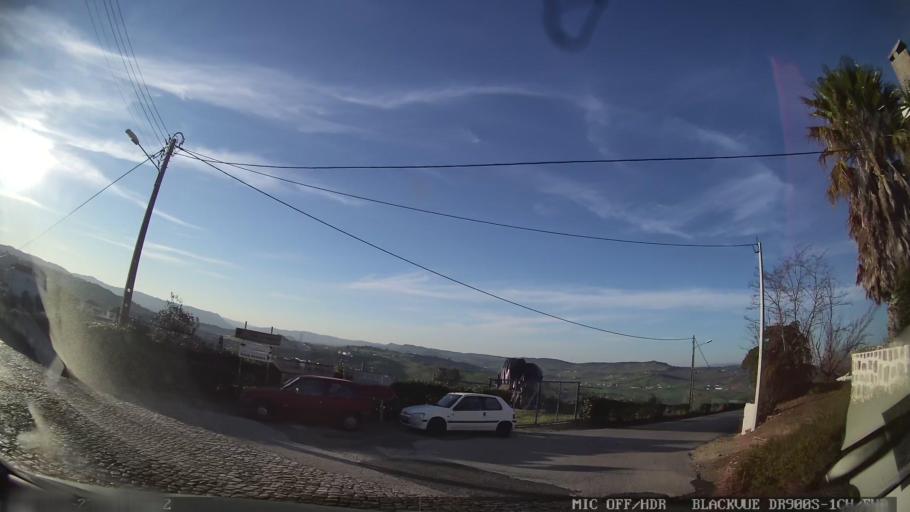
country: PT
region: Lisbon
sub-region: Vila Franca de Xira
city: Vila Franca de Xira
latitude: 38.9825
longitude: -9.0154
